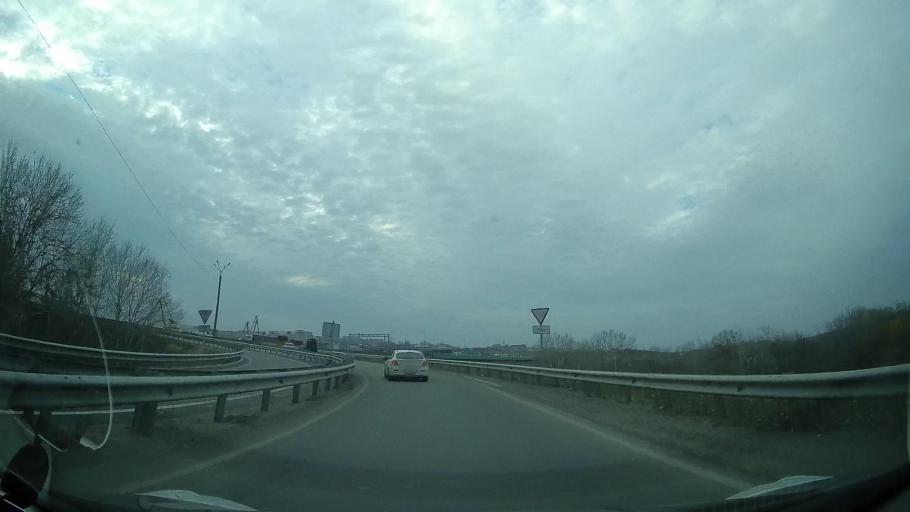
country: RU
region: Rostov
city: Aksay
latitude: 47.2396
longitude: 39.8567
